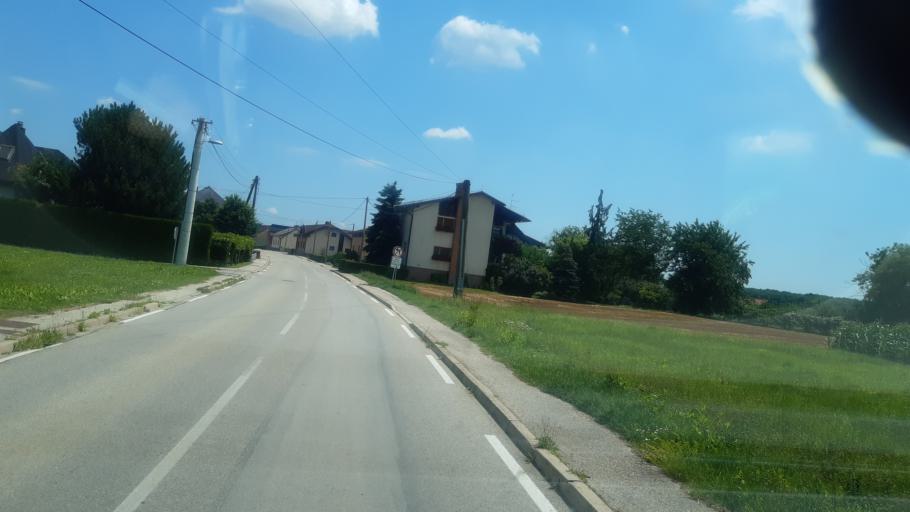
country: SI
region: Moravske Toplice
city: Moravske Toplice
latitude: 46.6688
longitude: 16.2221
